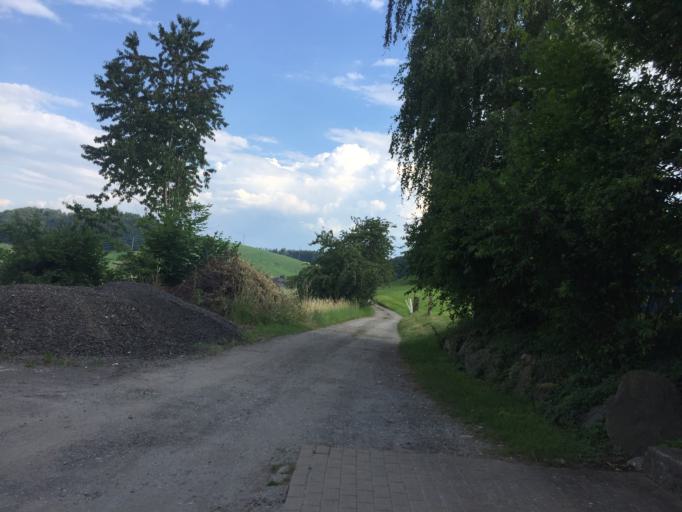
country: CH
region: Bern
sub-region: Bern-Mittelland District
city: Worb
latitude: 46.9337
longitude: 7.5490
